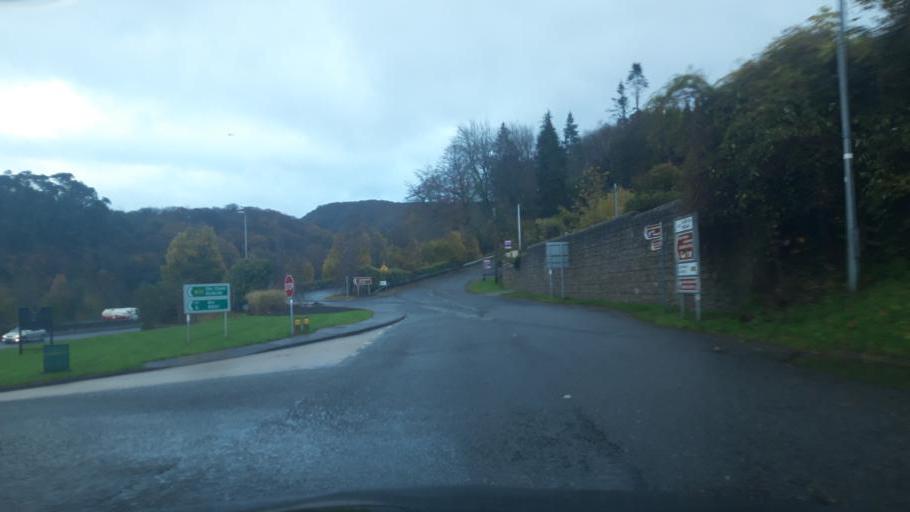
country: IE
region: Leinster
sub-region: Wicklow
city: Kilmacanoge
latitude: 53.1448
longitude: -6.1249
